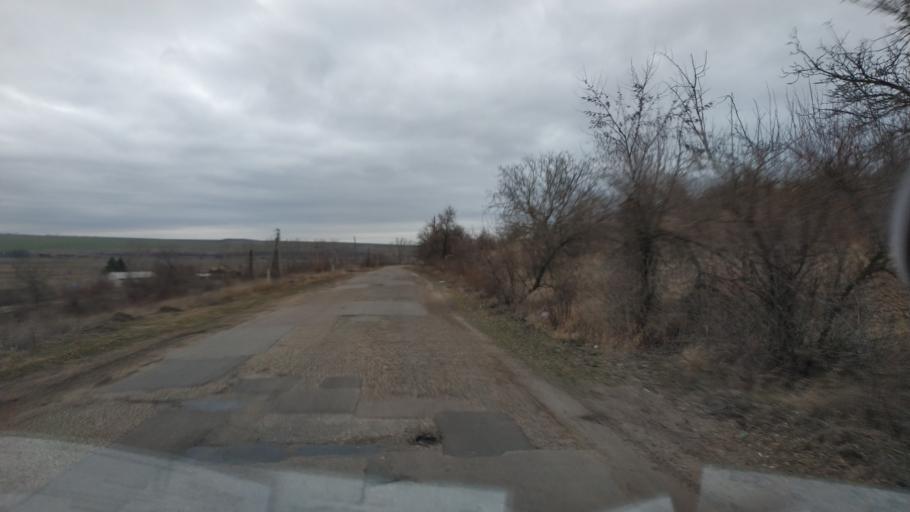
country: MD
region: Causeni
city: Causeni
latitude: 46.6656
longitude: 29.4550
